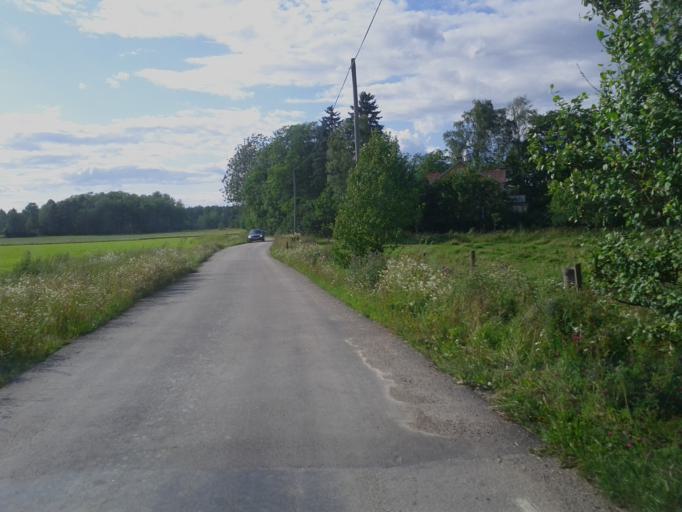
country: SE
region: Vaestmanland
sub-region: Sala Kommun
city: Sala
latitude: 59.9226
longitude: 16.4998
